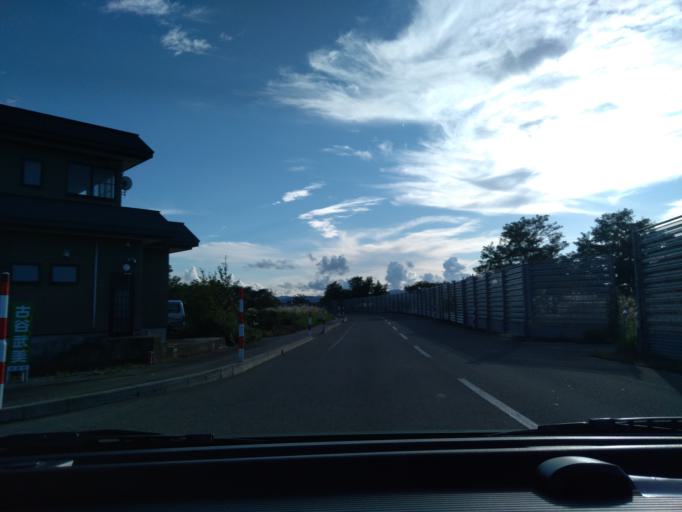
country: JP
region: Akita
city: Omagari
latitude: 39.4126
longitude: 140.4831
